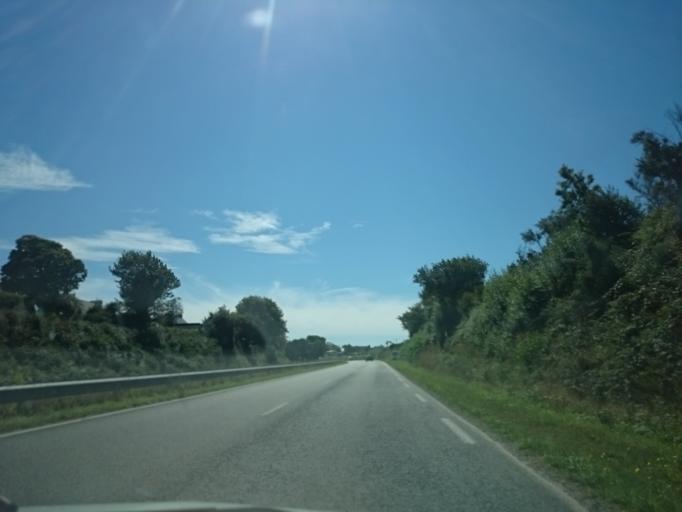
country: FR
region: Brittany
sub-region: Departement du Finistere
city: Guilers
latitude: 48.4215
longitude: -4.5654
